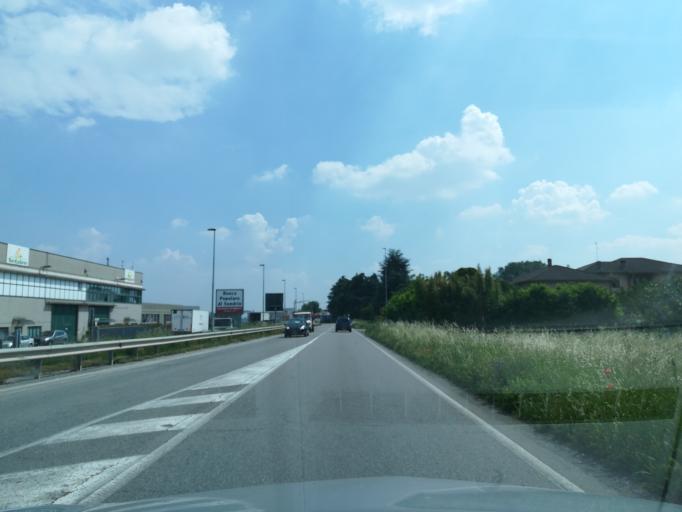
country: IT
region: Lombardy
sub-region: Provincia di Bergamo
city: Bolgare
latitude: 45.6467
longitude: 9.8079
